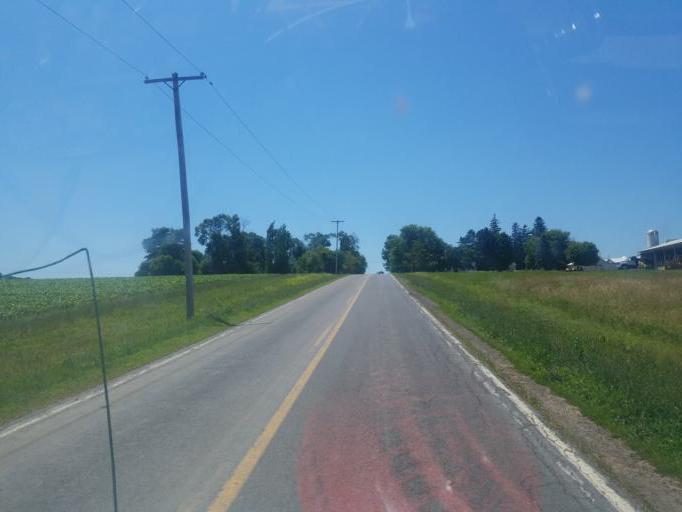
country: US
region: New York
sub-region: Ontario County
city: Geneva
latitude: 42.7991
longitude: -77.0154
